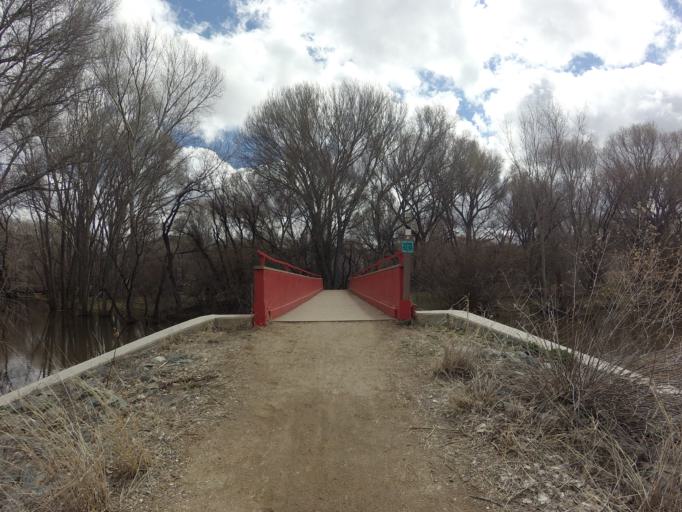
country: US
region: Arizona
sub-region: Yavapai County
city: Prescott
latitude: 34.5795
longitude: -112.4283
